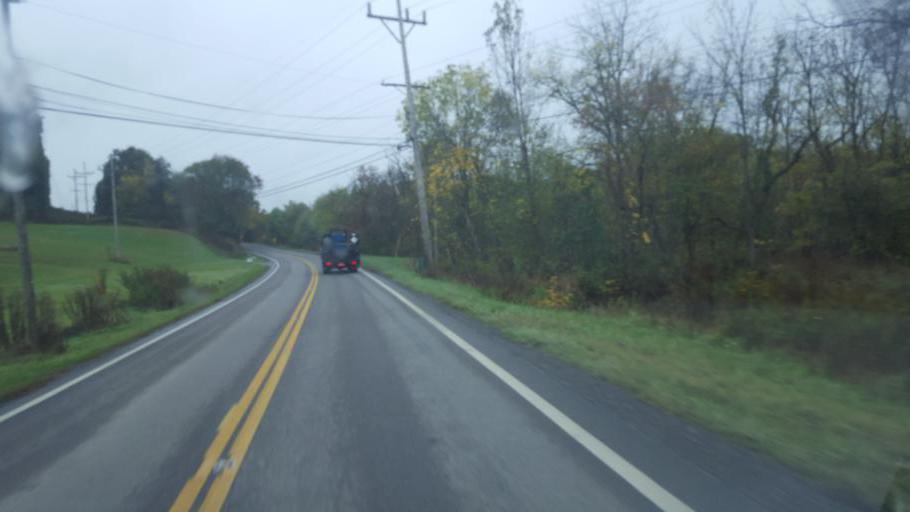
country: US
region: Ohio
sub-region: Tuscarawas County
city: Rockford
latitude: 40.4273
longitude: -81.1630
